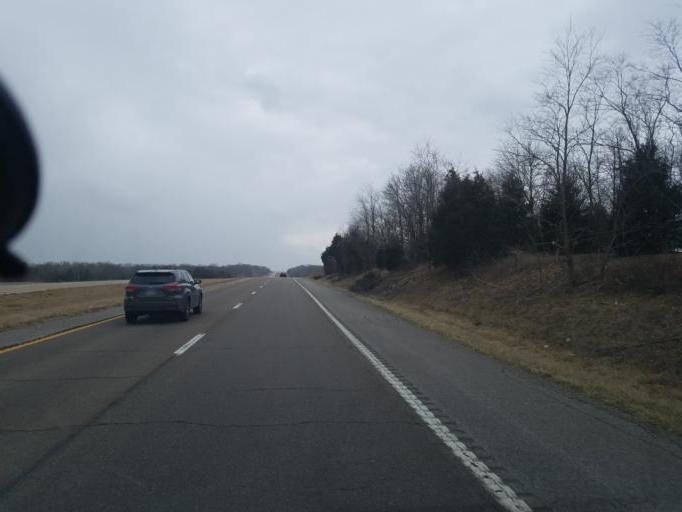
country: US
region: Missouri
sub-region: Boone County
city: Hallsville
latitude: 39.1098
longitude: -92.3292
